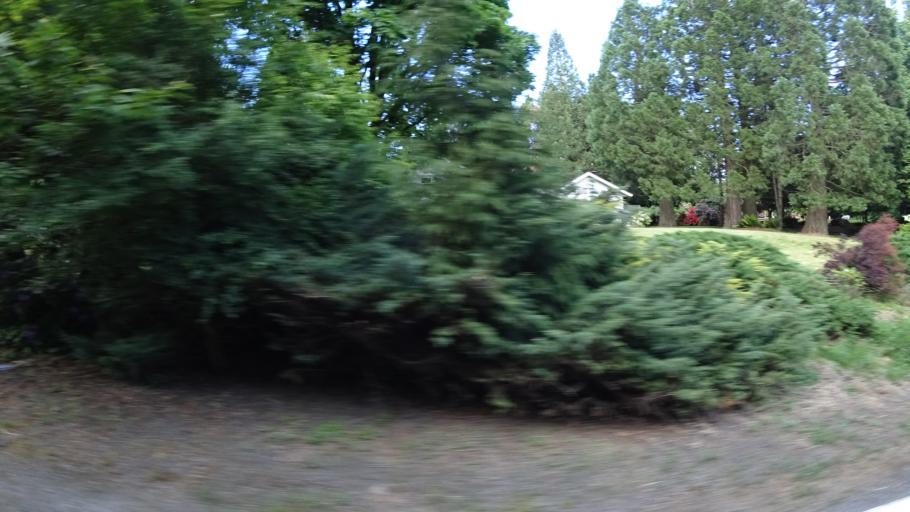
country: US
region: Oregon
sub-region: Washington County
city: Cedar Mill
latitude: 45.5725
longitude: -122.7908
